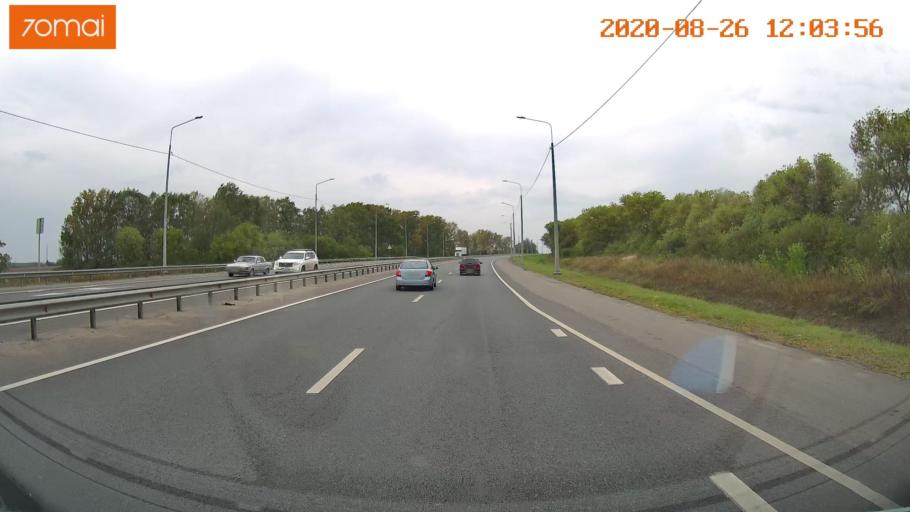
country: RU
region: Rjazan
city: Kiritsy
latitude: 54.3046
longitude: 40.1971
